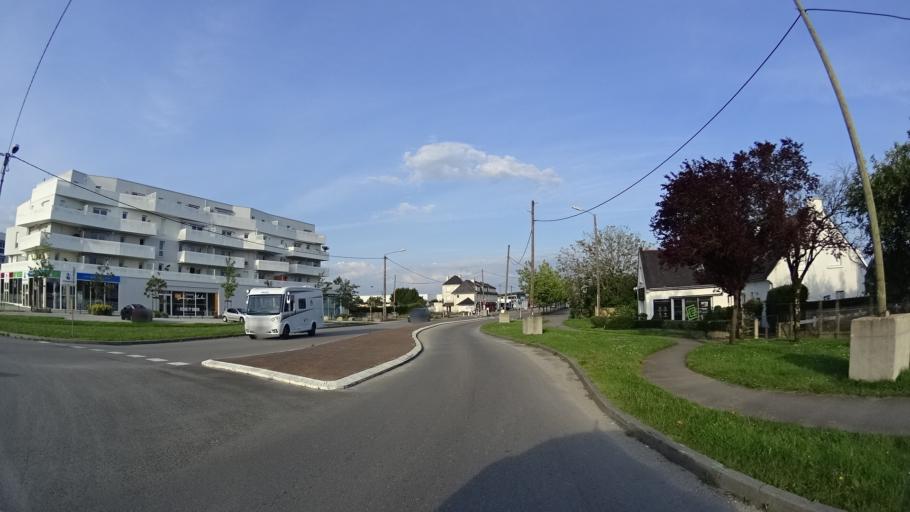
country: FR
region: Brittany
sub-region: Departement du Morbihan
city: Vannes
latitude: 47.6514
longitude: -2.7289
